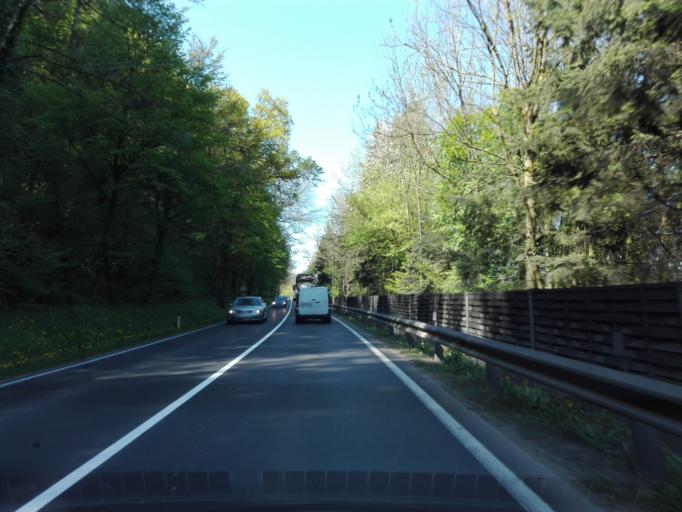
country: AT
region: Upper Austria
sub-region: Politischer Bezirk Linz-Land
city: Sankt Florian
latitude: 48.2434
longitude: 14.3614
